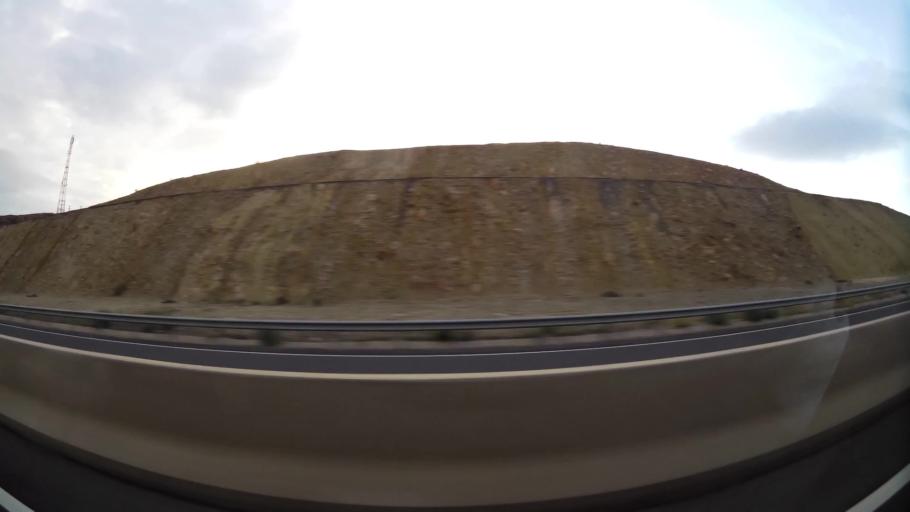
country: MA
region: Oriental
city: Taourirt
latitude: 34.4929
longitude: -2.9694
